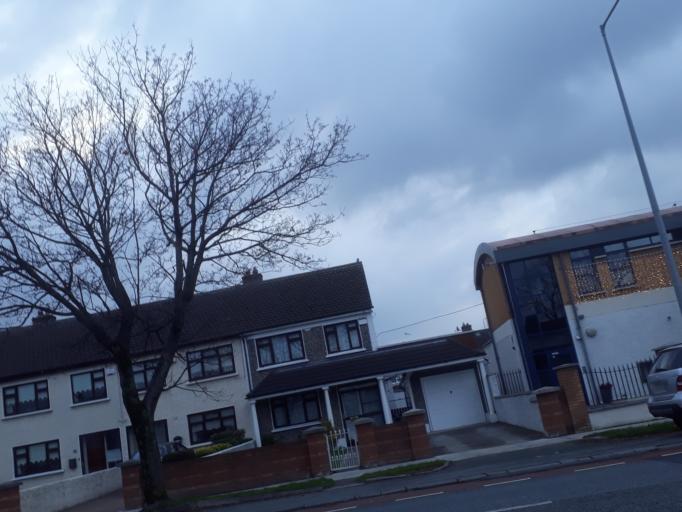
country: IE
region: Leinster
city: Crumlin
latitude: 53.3136
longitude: -6.3292
